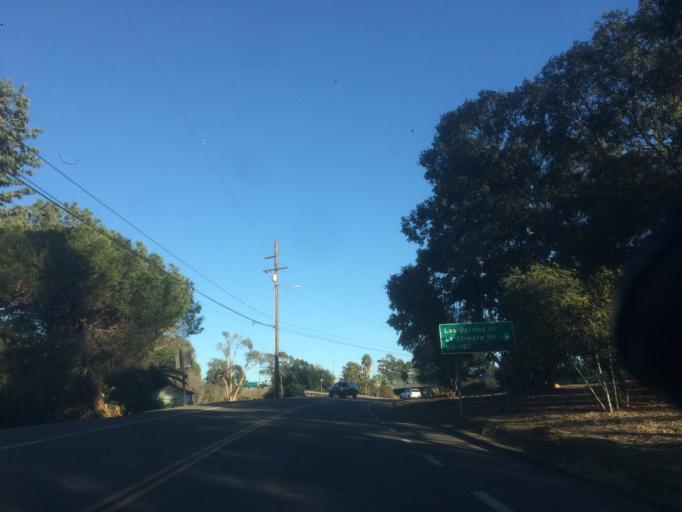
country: US
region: California
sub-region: Santa Barbara County
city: Mission Canyon
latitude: 34.4368
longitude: -119.7548
